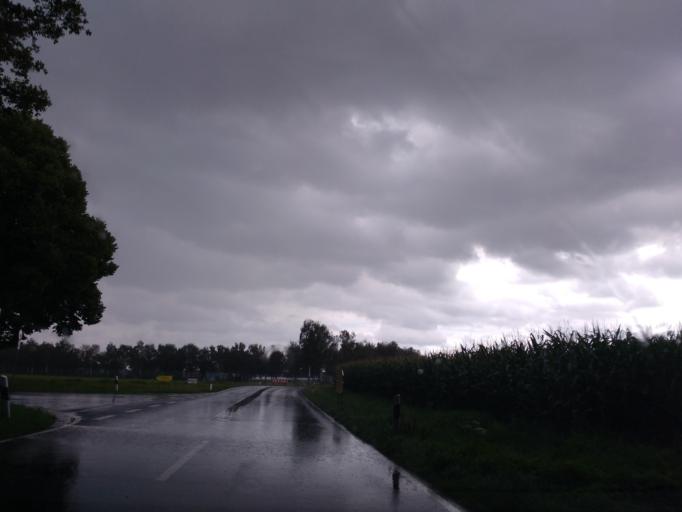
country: DE
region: North Rhine-Westphalia
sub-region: Regierungsbezirk Munster
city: Lienen
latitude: 52.1068
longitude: 7.9512
